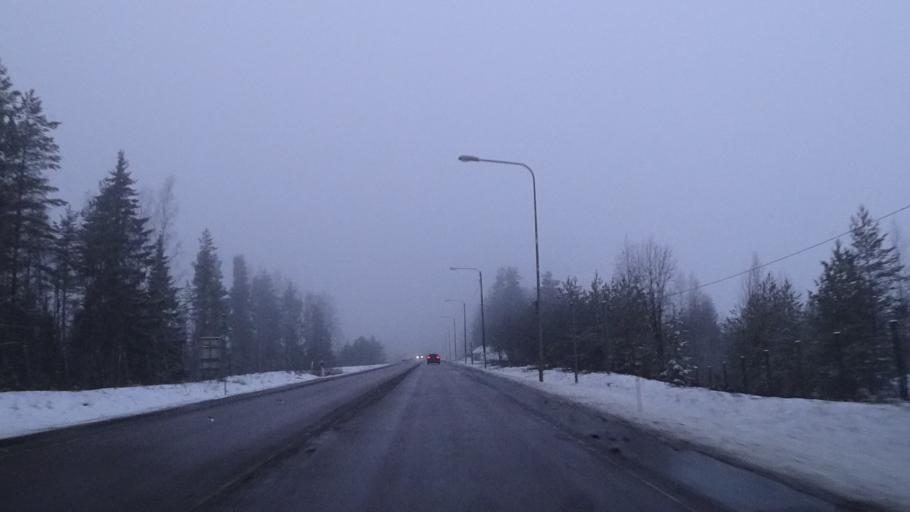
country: FI
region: Paijanne Tavastia
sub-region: Lahti
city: Hollola
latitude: 60.9864
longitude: 25.4028
